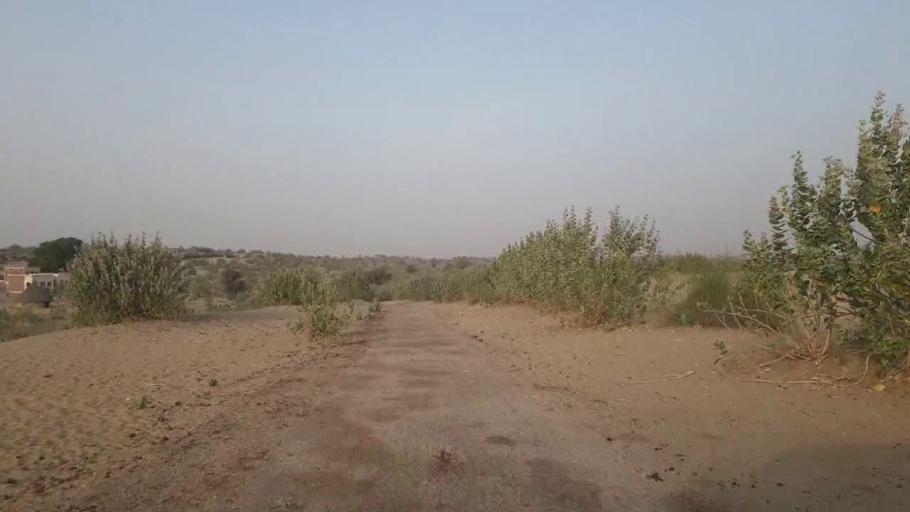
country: PK
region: Sindh
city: Chor
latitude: 25.5135
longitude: 69.9447
